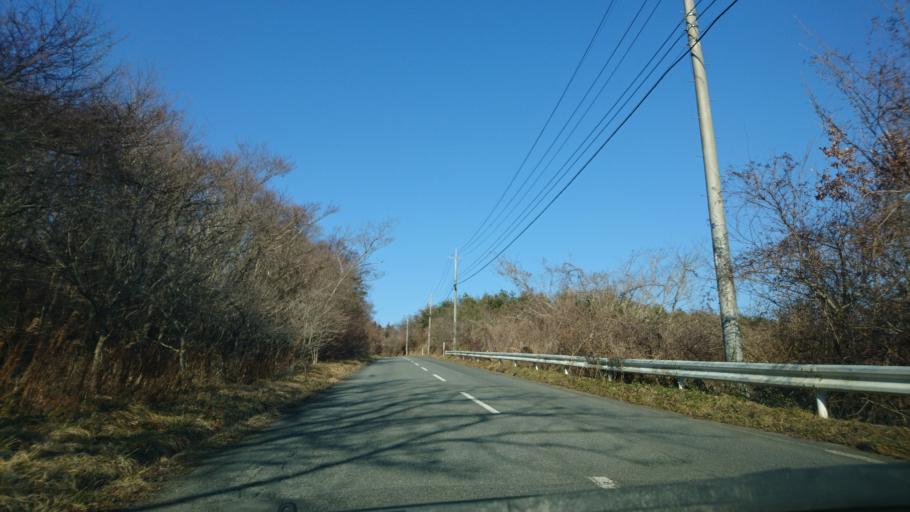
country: JP
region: Iwate
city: Ichinoseki
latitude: 38.8241
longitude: 141.2815
